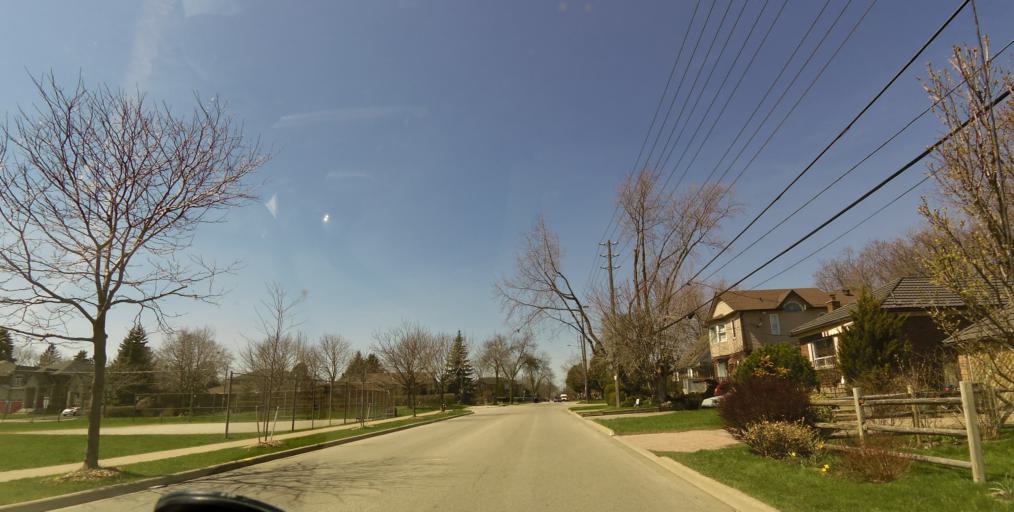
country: CA
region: Ontario
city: Etobicoke
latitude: 43.5824
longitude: -79.5664
